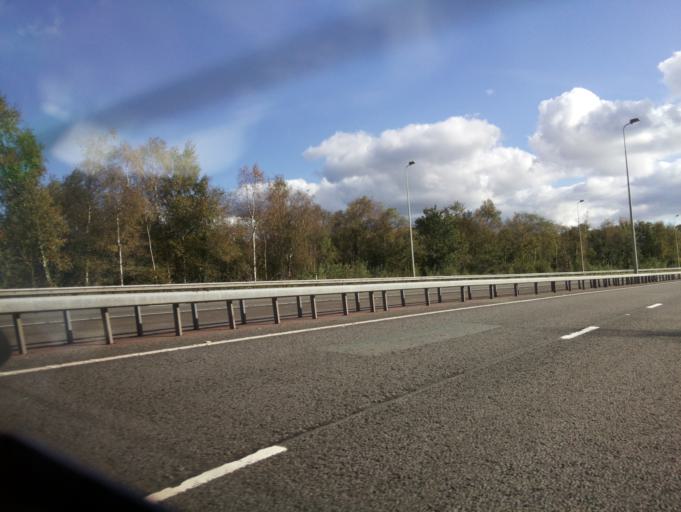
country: GB
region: Wales
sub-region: Merthyr Tydfil County Borough
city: Merthyr Tydfil
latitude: 51.7355
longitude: -3.3781
